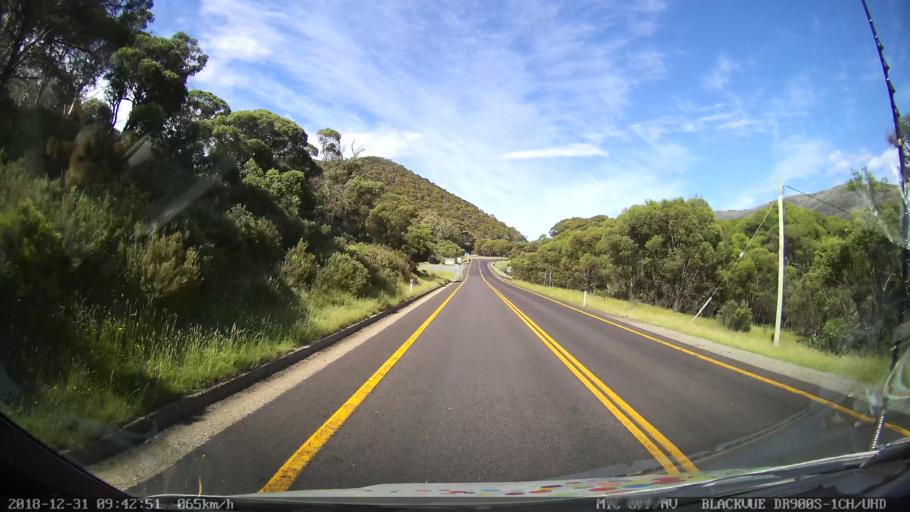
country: AU
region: New South Wales
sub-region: Snowy River
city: Jindabyne
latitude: -36.4989
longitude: 148.3186
